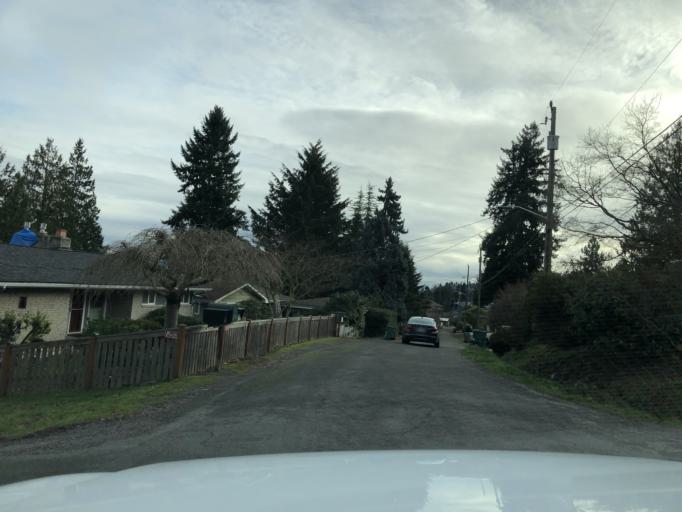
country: US
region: Washington
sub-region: King County
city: Inglewood-Finn Hill
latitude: 47.7076
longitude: -122.2769
